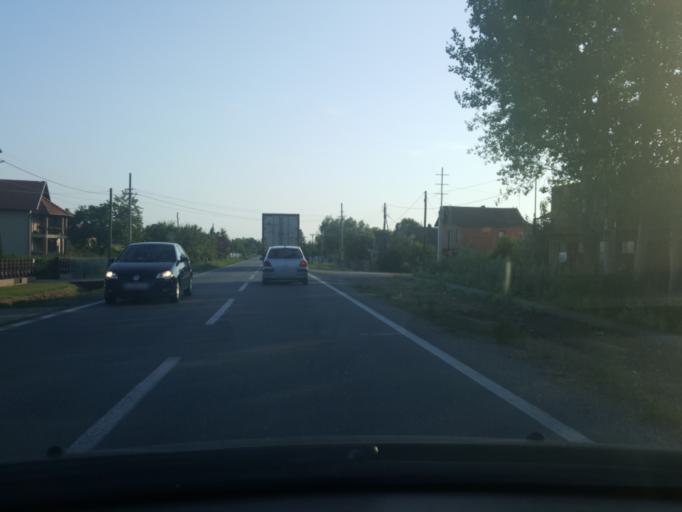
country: RS
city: Stitar
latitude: 44.7607
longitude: 19.5759
